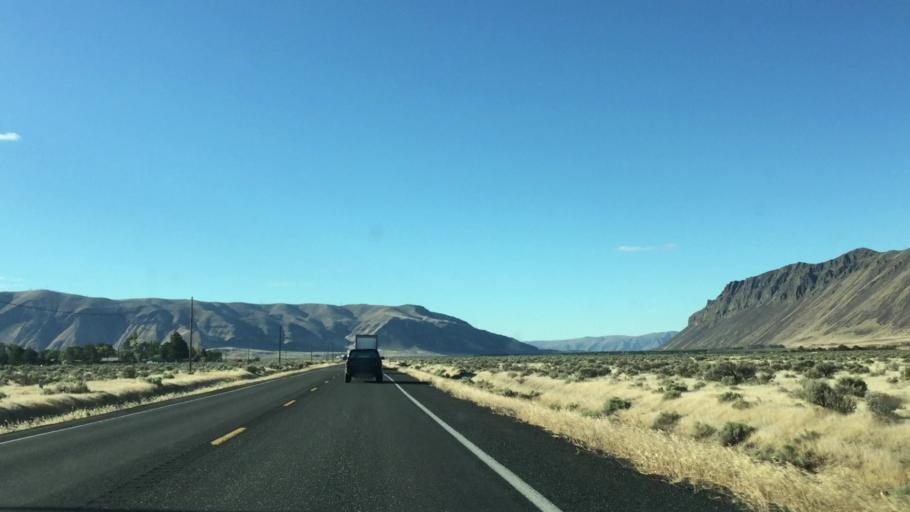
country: US
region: Washington
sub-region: Grant County
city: Mattawa
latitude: 46.8658
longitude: -119.9534
